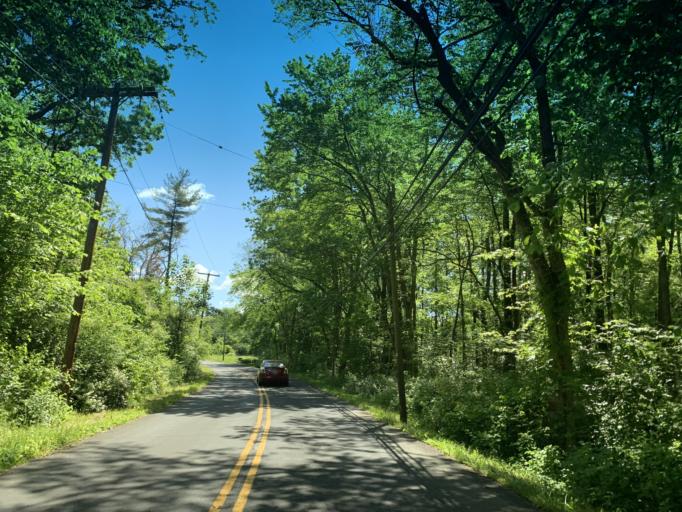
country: US
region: Maryland
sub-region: Harford County
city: South Bel Air
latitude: 39.6389
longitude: -76.2617
